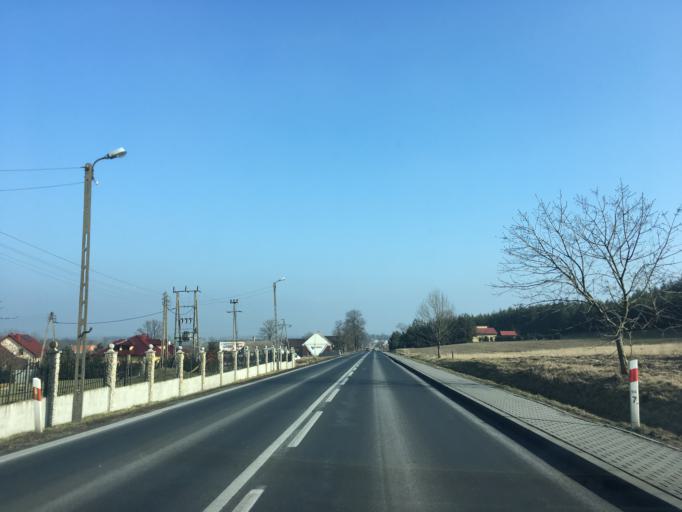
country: PL
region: Lower Silesian Voivodeship
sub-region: Powiat zlotoryjski
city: Olszanica
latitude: 51.2697
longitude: 15.7567
